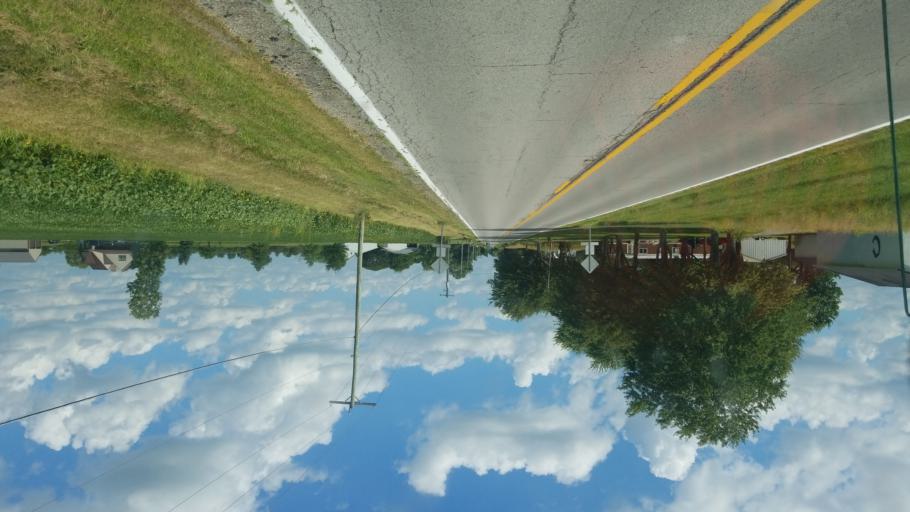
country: US
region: Ohio
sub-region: Union County
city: Richwood
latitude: 40.3982
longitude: -83.2823
